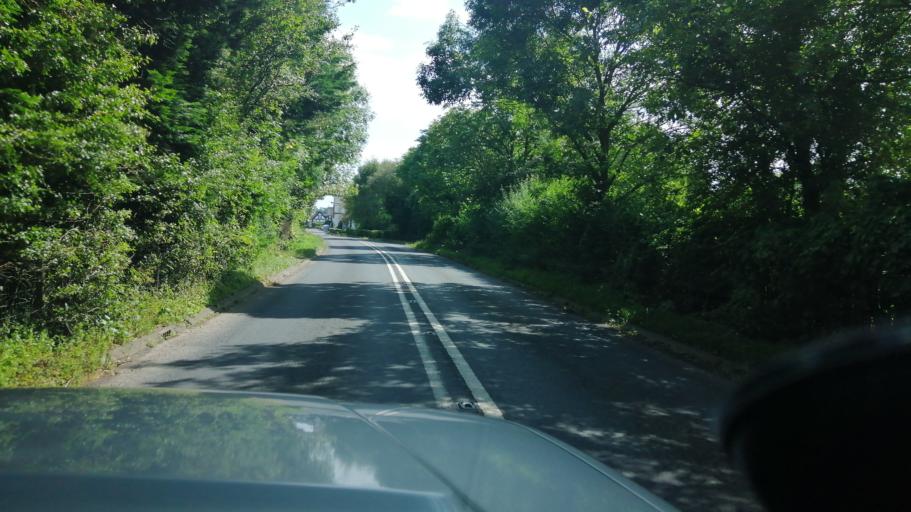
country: GB
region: England
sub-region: Herefordshire
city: Kinnersley
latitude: 52.1123
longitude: -2.9685
